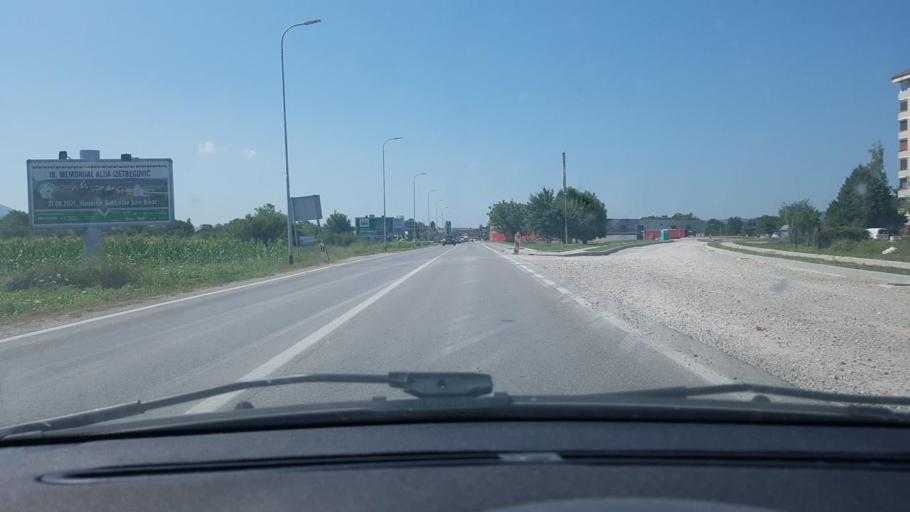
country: BA
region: Federation of Bosnia and Herzegovina
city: Bihac
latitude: 44.8105
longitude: 15.8825
